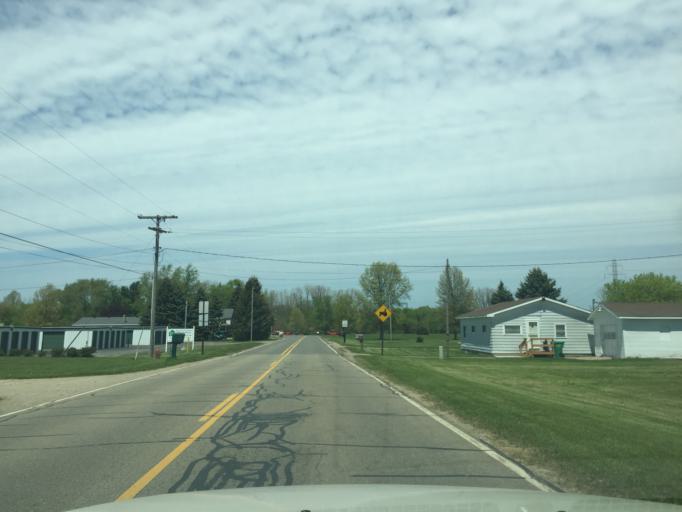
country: US
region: Michigan
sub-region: Berrien County
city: Stevensville
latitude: 41.9605
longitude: -86.4863
